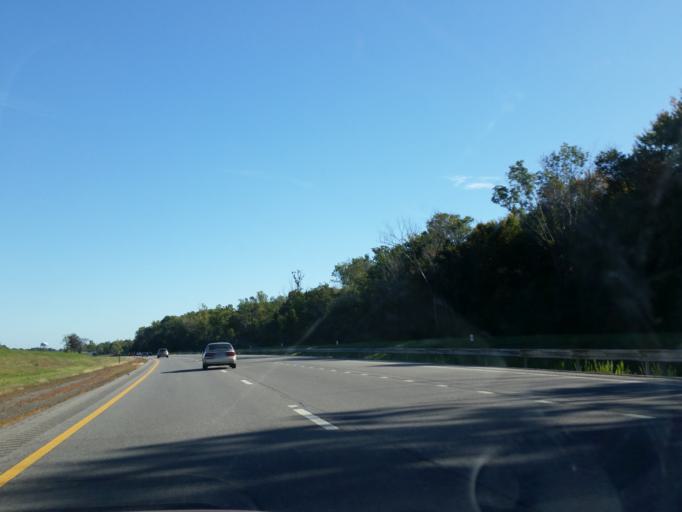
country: US
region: New York
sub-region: Erie County
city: Hamburg
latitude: 42.7443
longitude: -78.8394
